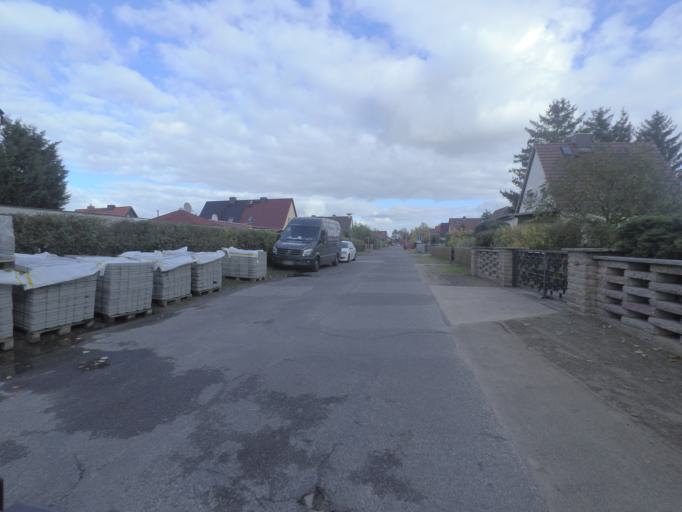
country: DE
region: Brandenburg
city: Ludwigsfelde
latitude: 52.2928
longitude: 13.2520
